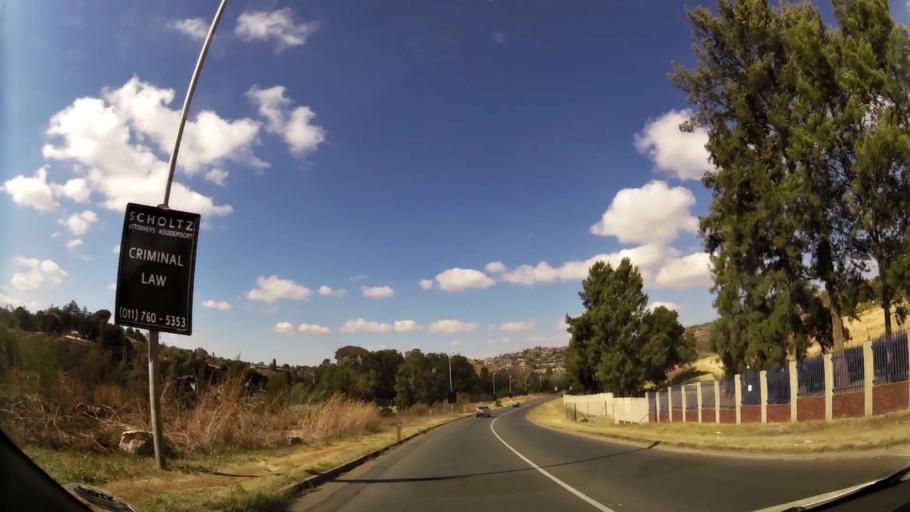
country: ZA
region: Gauteng
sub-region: West Rand District Municipality
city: Krugersdorp
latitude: -26.1034
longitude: 27.8381
